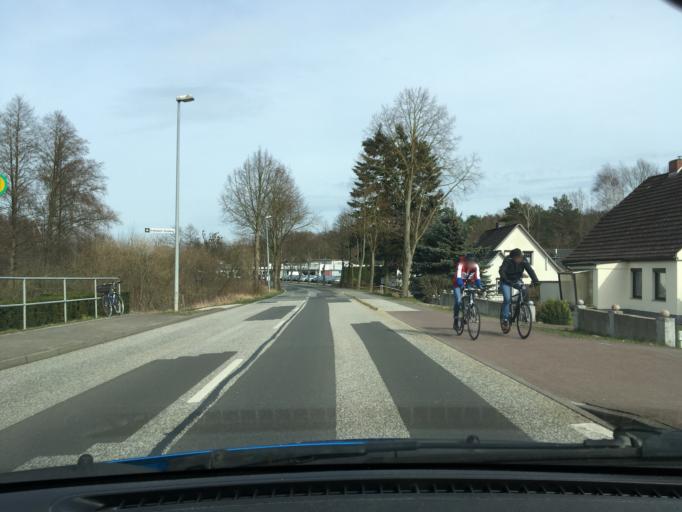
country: DE
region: Mecklenburg-Vorpommern
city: Feldstadt
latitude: 53.5941
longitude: 11.4122
